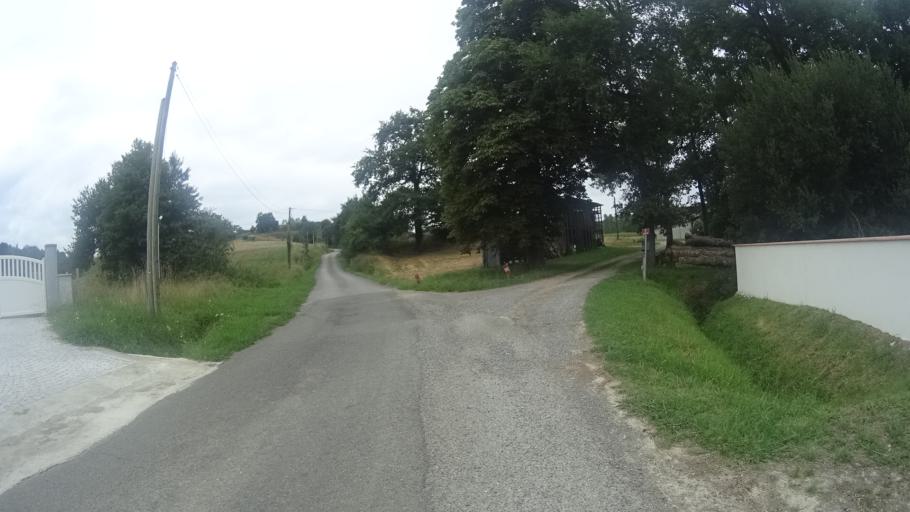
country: FR
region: Aquitaine
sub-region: Departement des Pyrenees-Atlantiques
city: Mont
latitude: 43.4889
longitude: -0.6943
